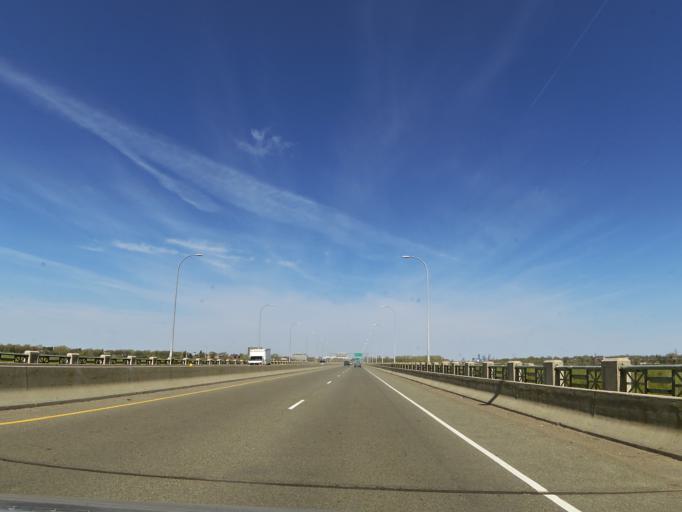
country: US
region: Minnesota
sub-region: Dakota County
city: Mendota Heights
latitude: 44.8841
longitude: -93.1721
